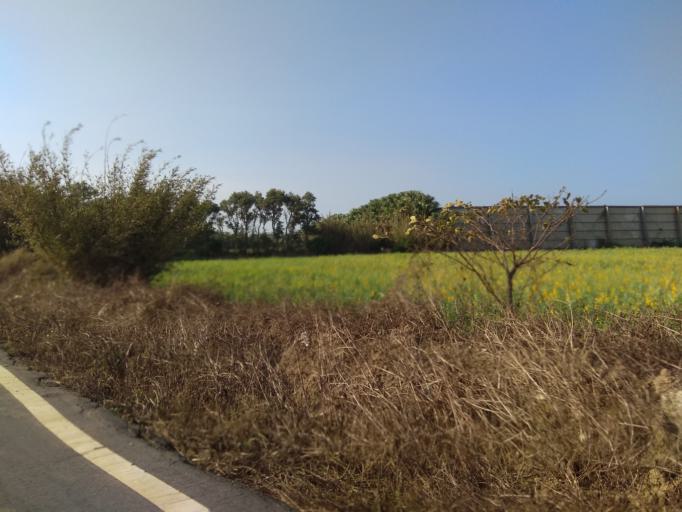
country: TW
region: Taiwan
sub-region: Hsinchu
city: Zhubei
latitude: 25.0036
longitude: 121.0462
